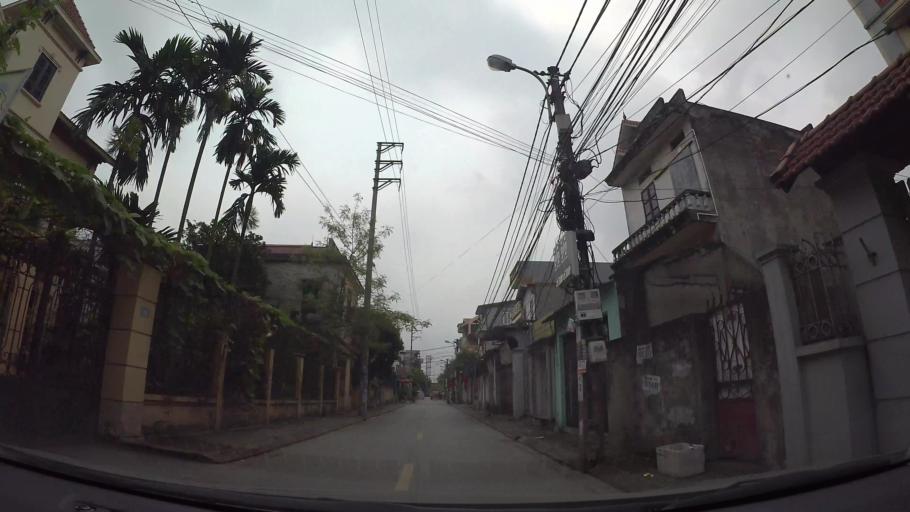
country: VN
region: Ha Noi
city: Trau Quy
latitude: 21.0615
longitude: 105.9183
